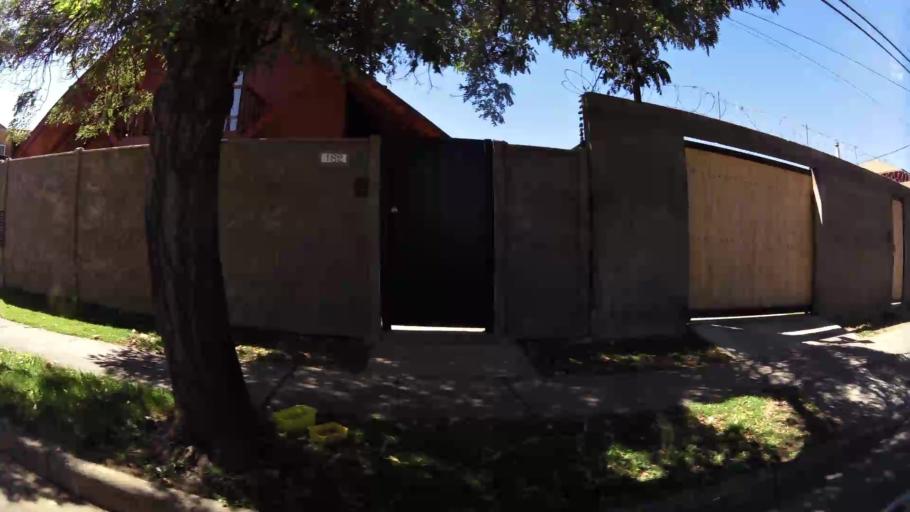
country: CL
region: O'Higgins
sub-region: Provincia de Cachapoal
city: Rancagua
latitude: -34.1766
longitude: -70.7141
